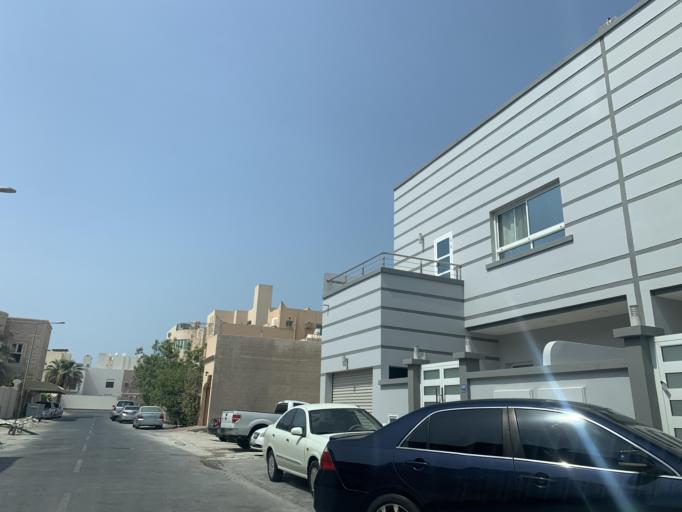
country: BH
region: Muharraq
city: Al Hadd
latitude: 26.2662
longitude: 50.6598
